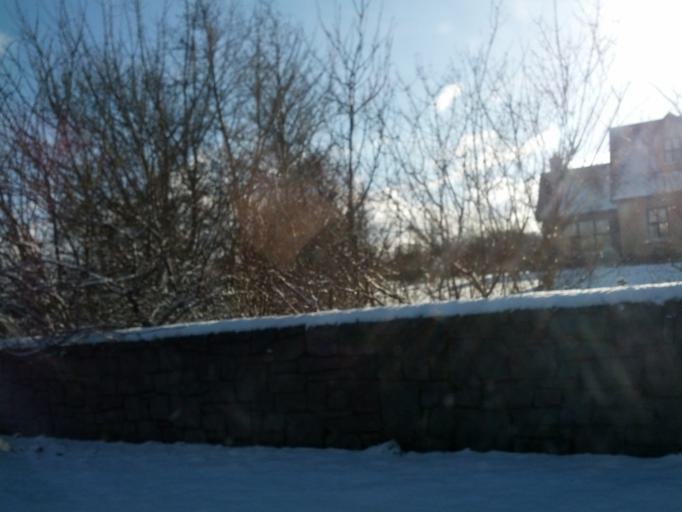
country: IE
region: Connaught
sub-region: County Galway
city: Athenry
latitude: 53.1893
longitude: -8.7888
